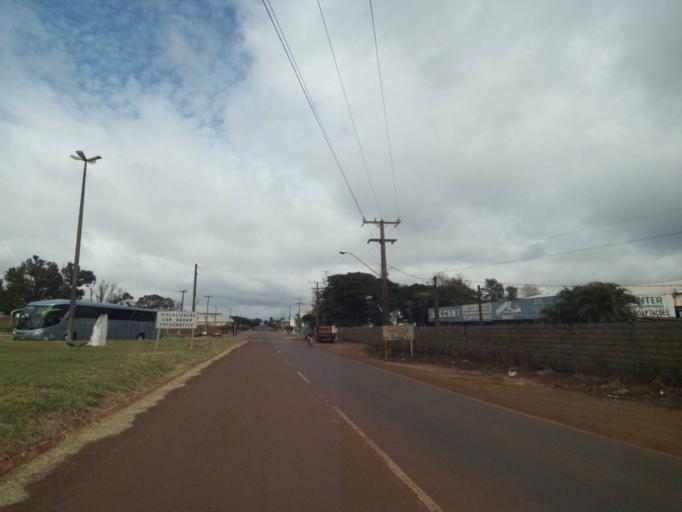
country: BR
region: Parana
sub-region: Campo Mourao
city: Campo Mourao
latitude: -24.0201
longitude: -52.3641
